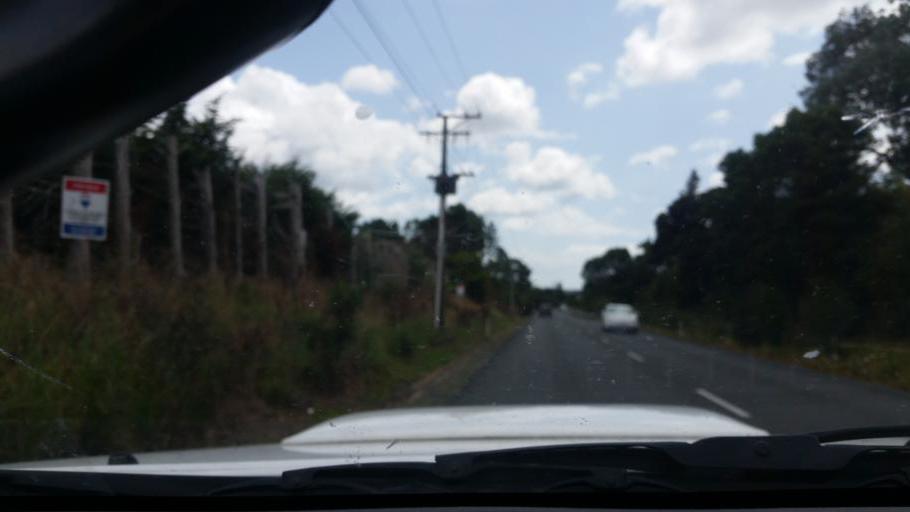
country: NZ
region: Auckland
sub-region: Auckland
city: Wellsford
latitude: -36.1200
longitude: 174.5726
